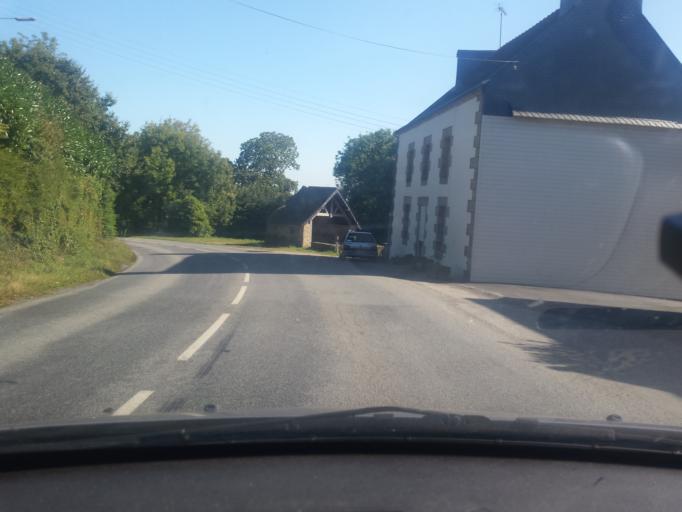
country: FR
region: Brittany
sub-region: Departement du Morbihan
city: Guemene-sur-Scorff
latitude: 48.1351
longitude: -3.1539
